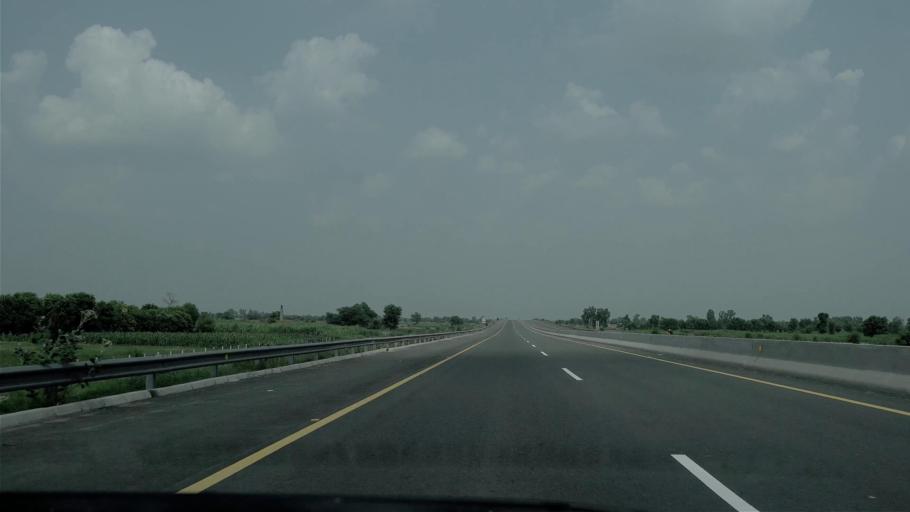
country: PK
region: Punjab
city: Gojra
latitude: 31.1936
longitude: 72.6522
